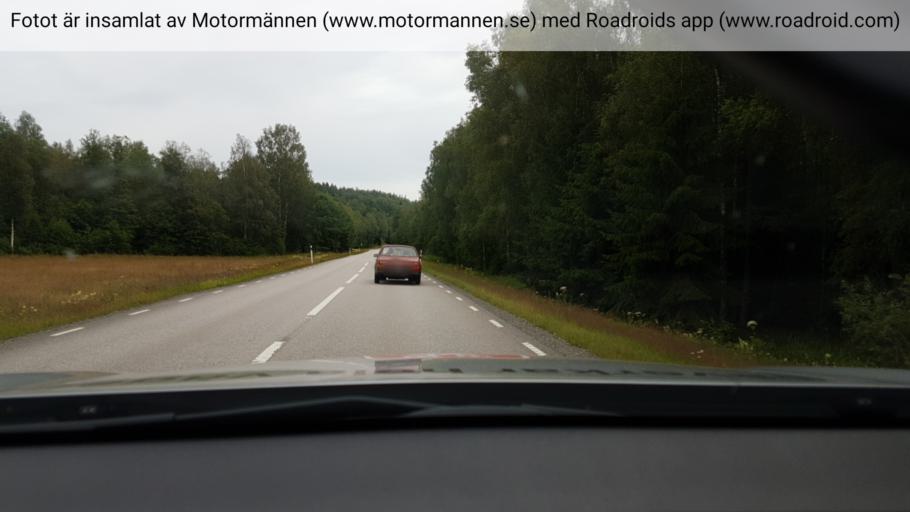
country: SE
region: Vaestra Goetaland
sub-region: Bengtsfors Kommun
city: Dals Langed
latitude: 58.8828
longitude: 12.2114
